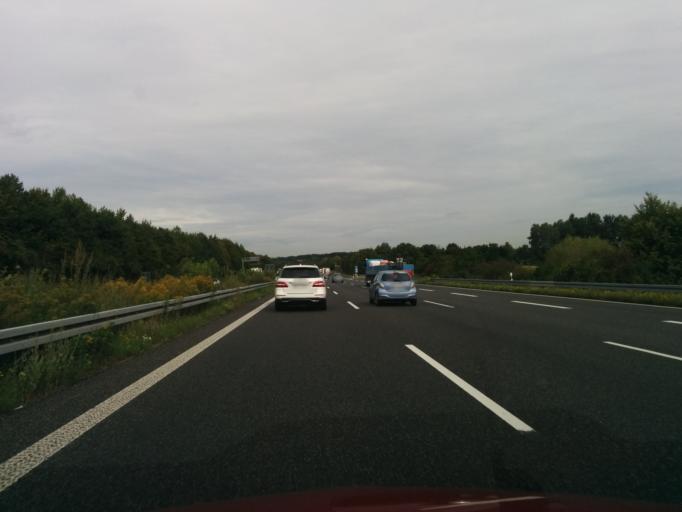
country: DE
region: Baden-Wuerttemberg
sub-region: Karlsruhe Region
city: Ettlingen
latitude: 48.9536
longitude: 8.4843
